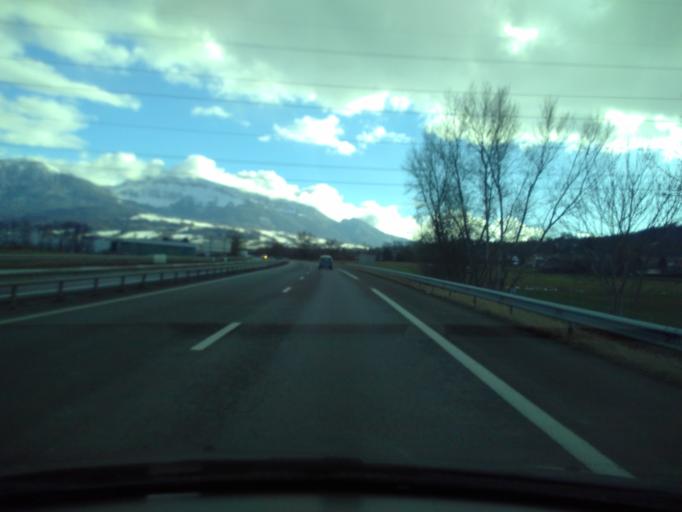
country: FR
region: Rhone-Alpes
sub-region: Departement de la Haute-Savoie
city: Cornier
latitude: 46.0840
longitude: 6.2882
